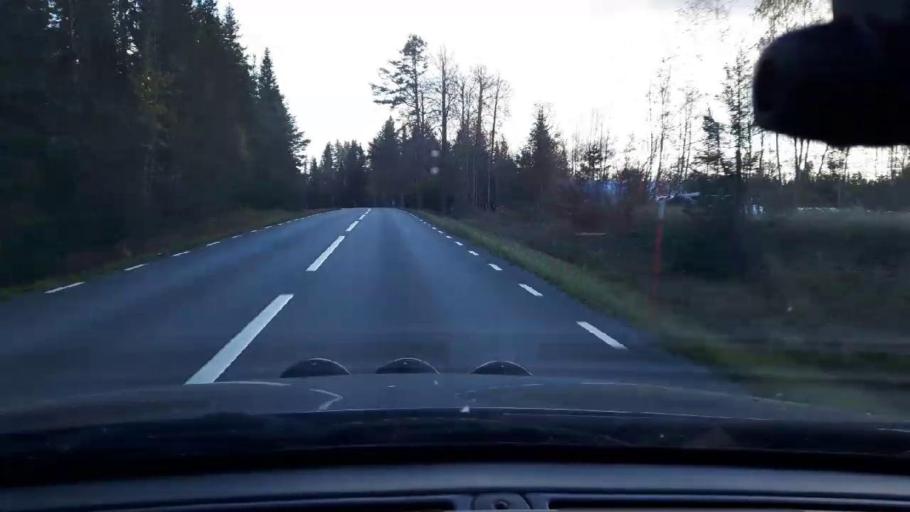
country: SE
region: Jaemtland
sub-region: Bergs Kommun
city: Hoverberg
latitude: 63.0532
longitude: 14.3272
